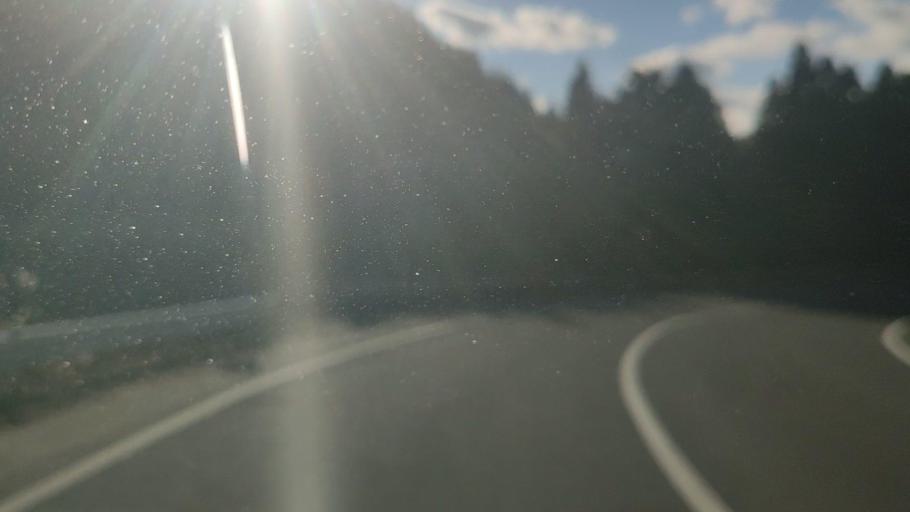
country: JP
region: Saga Prefecture
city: Kanzakimachi-kanzaki
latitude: 33.3928
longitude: 130.2701
